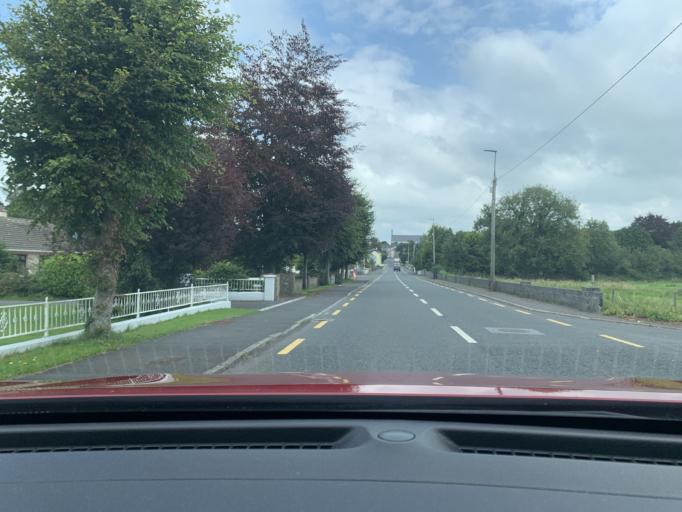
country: IE
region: Connaught
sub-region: Maigh Eo
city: Kiltamagh
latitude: 53.8451
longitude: -9.0069
